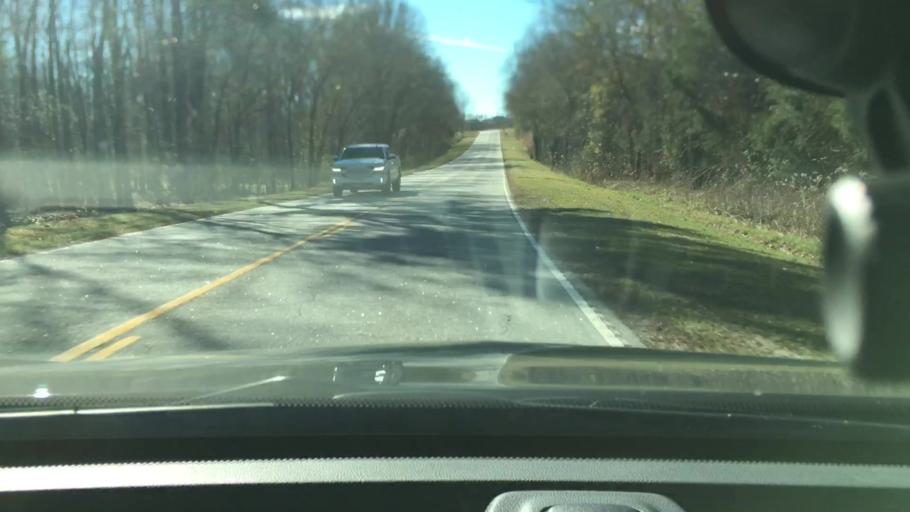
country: US
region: South Carolina
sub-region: Cherokee County
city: Gaffney
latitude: 35.0097
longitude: -81.6880
